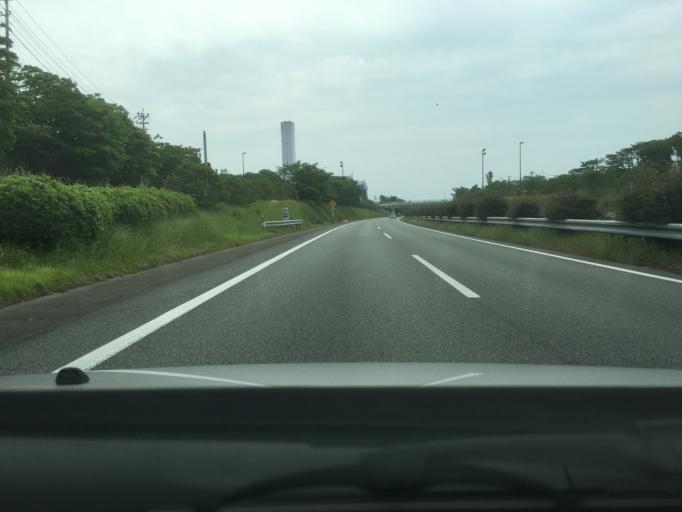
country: JP
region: Kumamoto
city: Ozu
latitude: 32.8109
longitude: 130.7936
